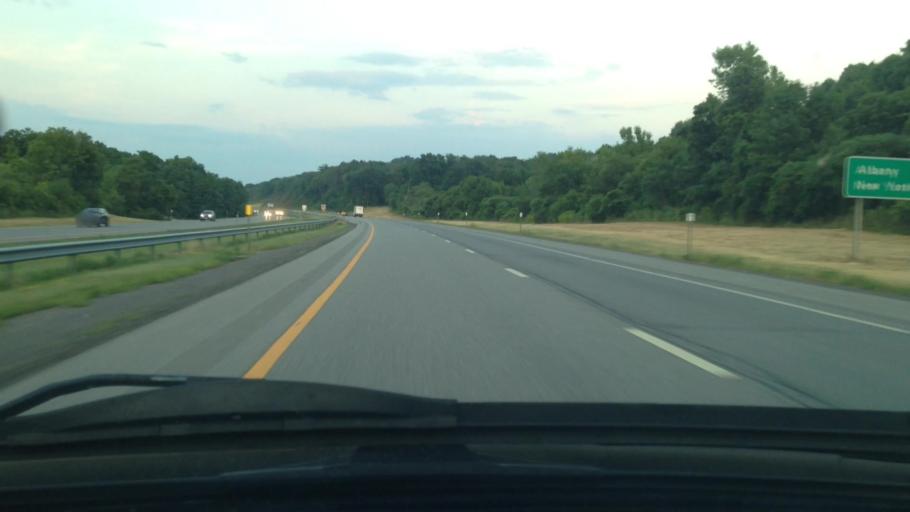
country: US
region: New York
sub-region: Montgomery County
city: Saint Johnsville
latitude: 42.9896
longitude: -74.7241
